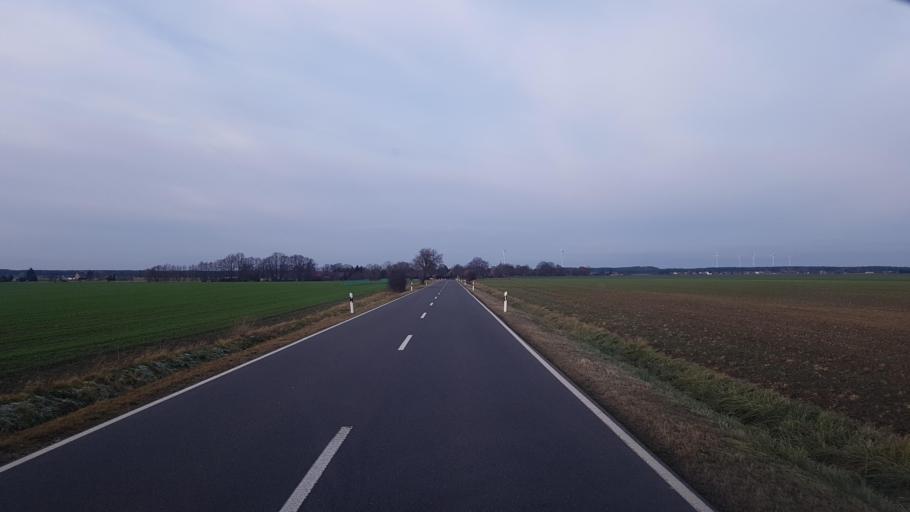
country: DE
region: Brandenburg
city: Doberlug-Kirchhain
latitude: 51.6645
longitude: 13.5191
